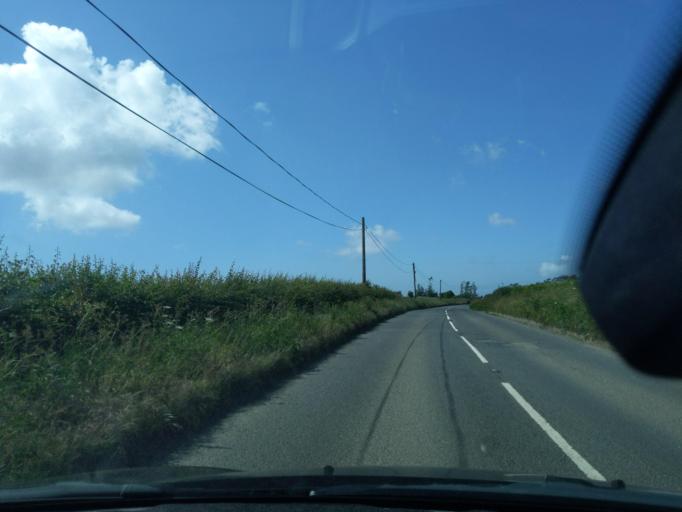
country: GB
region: England
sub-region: Devon
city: Great Torrington
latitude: 51.0005
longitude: -4.1009
